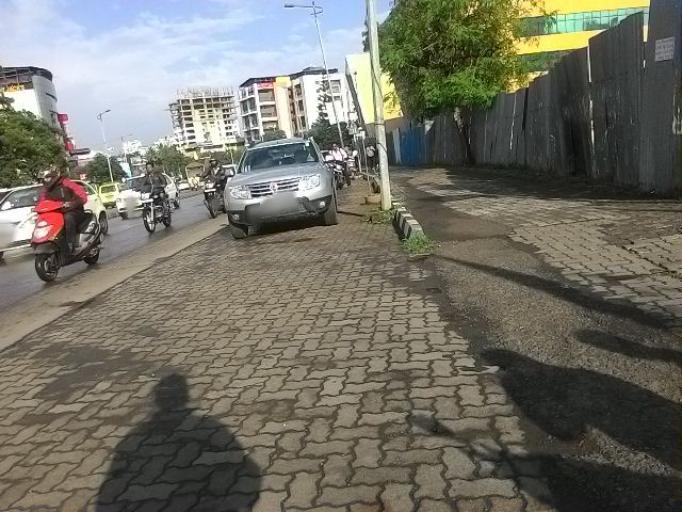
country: IN
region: Maharashtra
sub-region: Pune Division
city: Khadki
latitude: 18.5550
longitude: 73.7959
